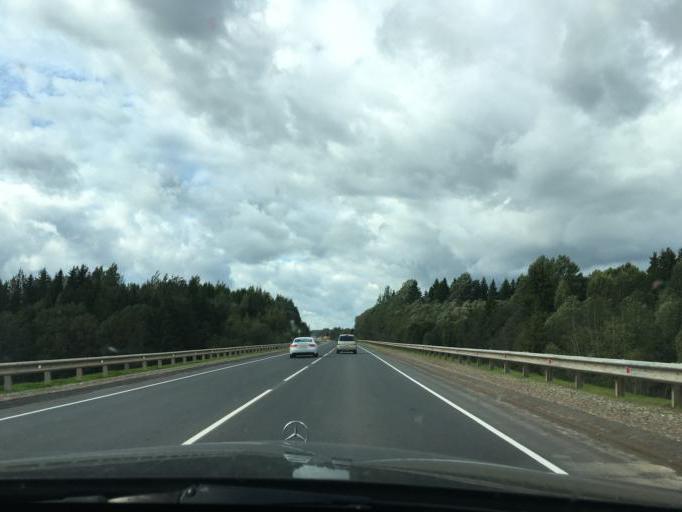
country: RU
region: Tverskaya
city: Toropets
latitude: 56.3302
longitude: 31.2255
